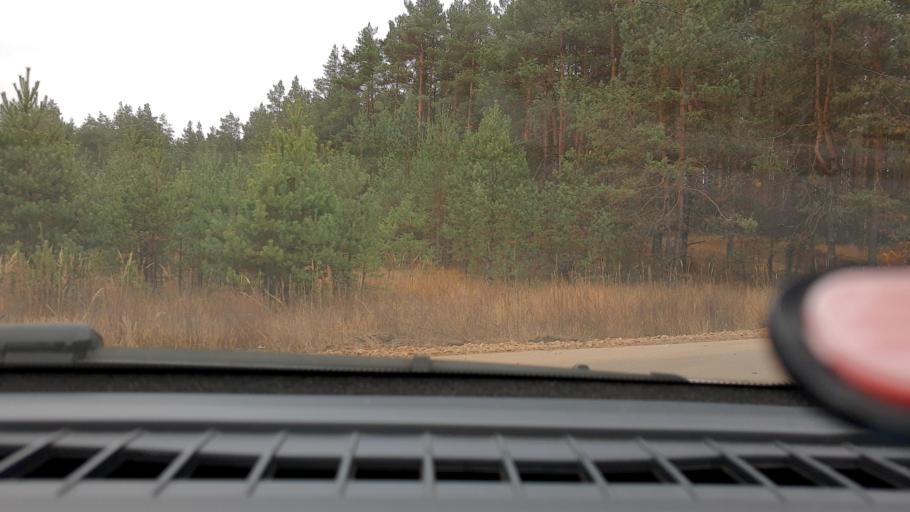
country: RU
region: Nizjnij Novgorod
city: Lukino
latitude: 56.3898
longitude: 43.7177
